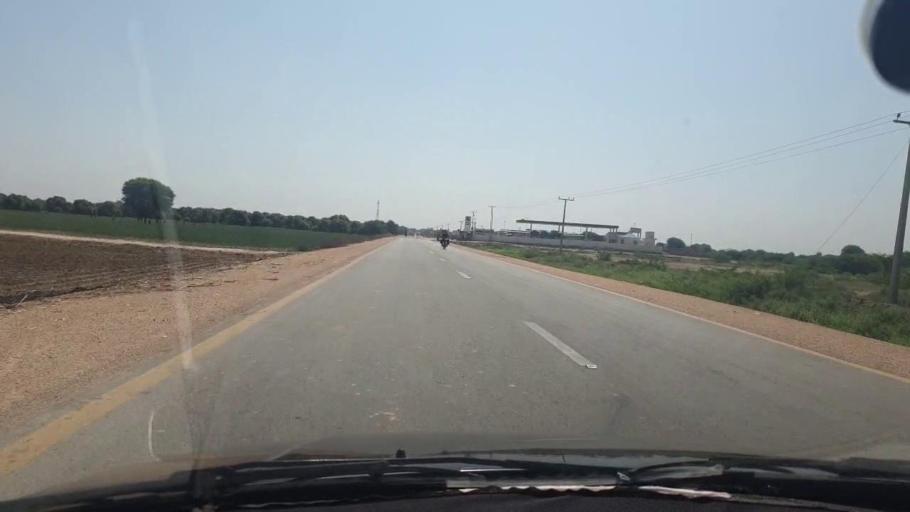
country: PK
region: Sindh
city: Chambar
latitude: 25.3108
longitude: 68.8064
